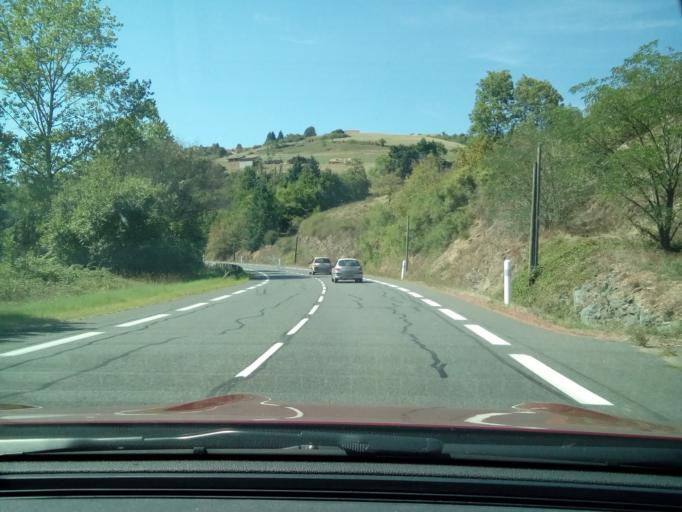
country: FR
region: Rhone-Alpes
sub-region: Departement du Rhone
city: Pontcharra-sur-Turdine
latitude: 45.9223
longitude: 4.4799
